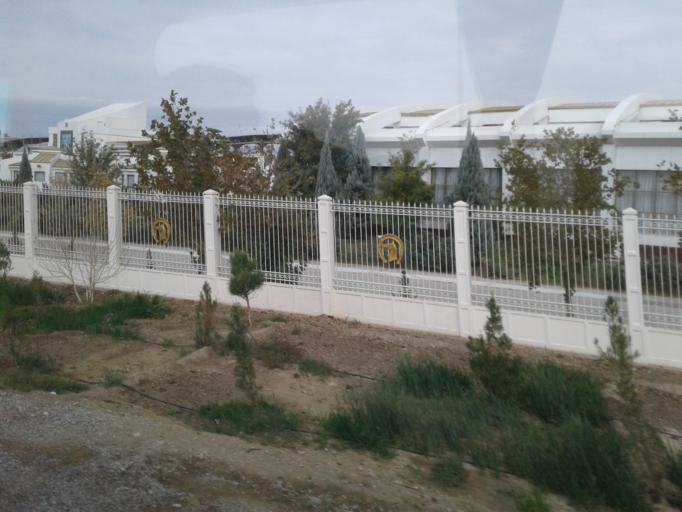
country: TM
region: Lebap
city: Turkmenabat
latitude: 38.9890
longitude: 63.5620
